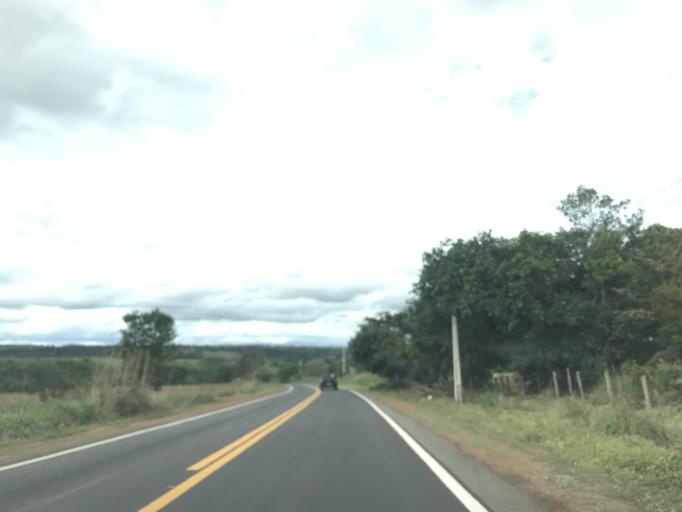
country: BR
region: Goias
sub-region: Bela Vista De Goias
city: Bela Vista de Goias
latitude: -17.1741
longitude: -48.6830
